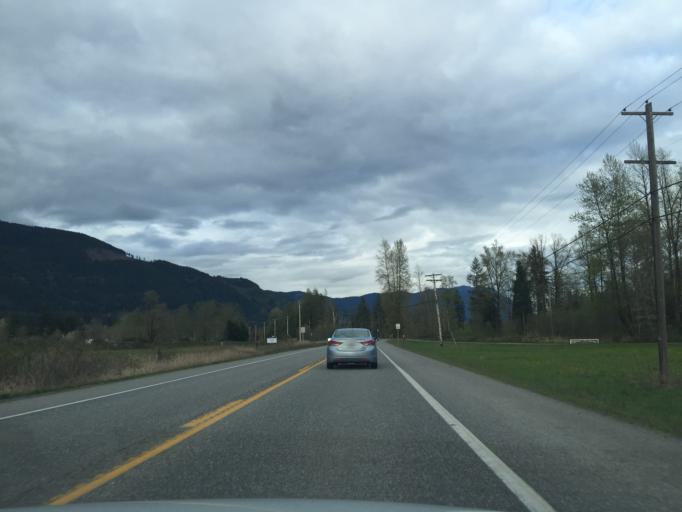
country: US
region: Washington
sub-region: Snohomish County
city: Arlington Heights
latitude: 48.2696
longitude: -122.0065
